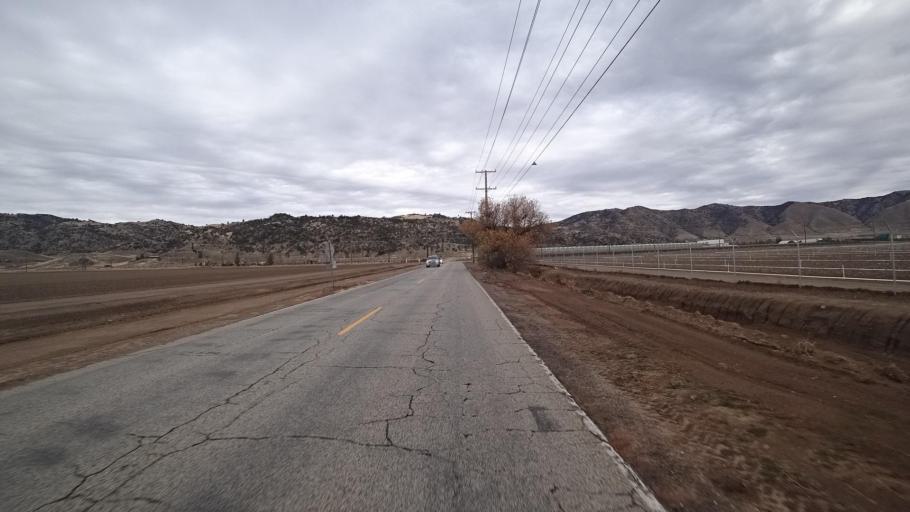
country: US
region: California
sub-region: Kern County
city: Bear Valley Springs
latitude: 35.1223
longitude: -118.6020
